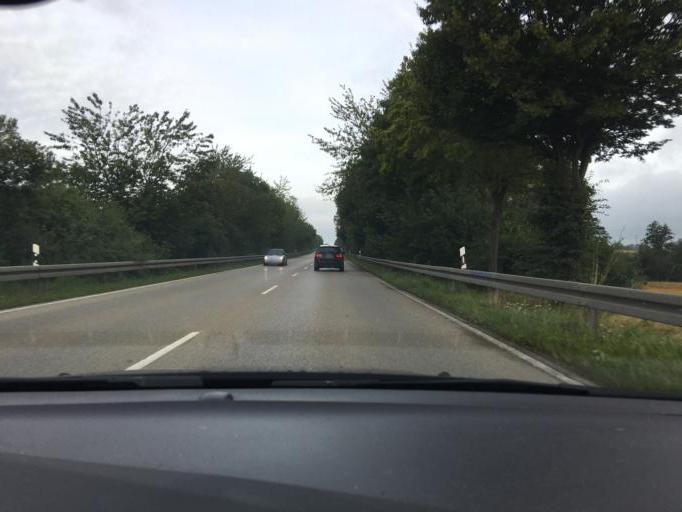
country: DE
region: Bavaria
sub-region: Upper Bavaria
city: Stammham
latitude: 48.2847
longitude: 11.8852
